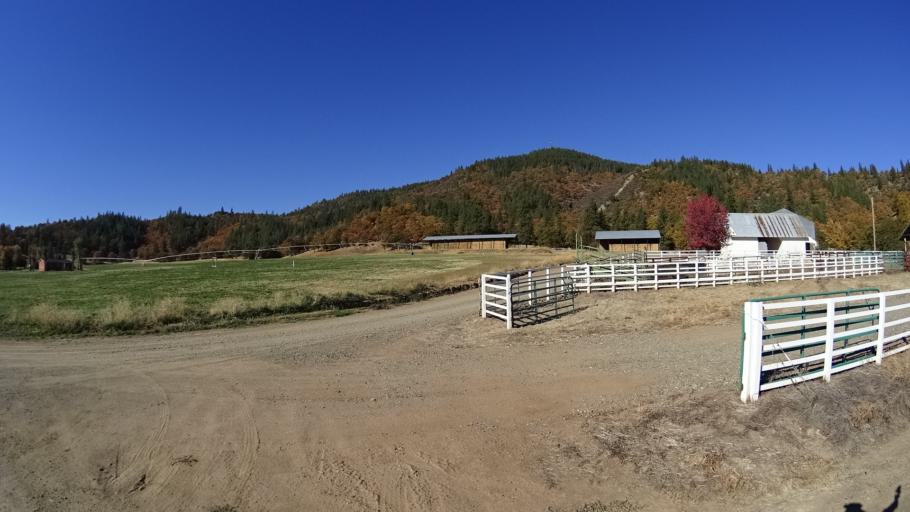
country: US
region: California
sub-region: Siskiyou County
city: Yreka
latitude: 41.5934
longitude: -122.8585
